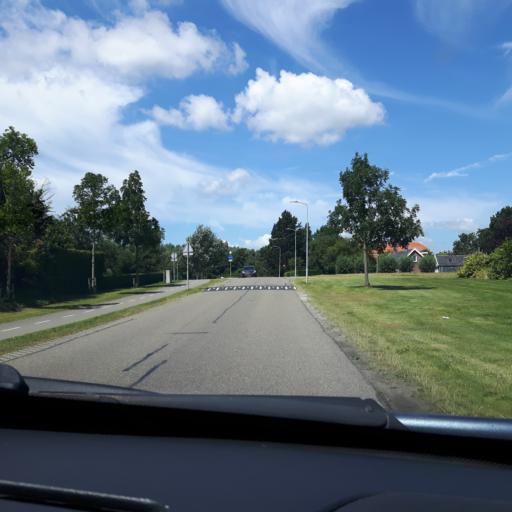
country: NL
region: Zeeland
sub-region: Gemeente Goes
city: Goes
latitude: 51.5221
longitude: 3.9097
